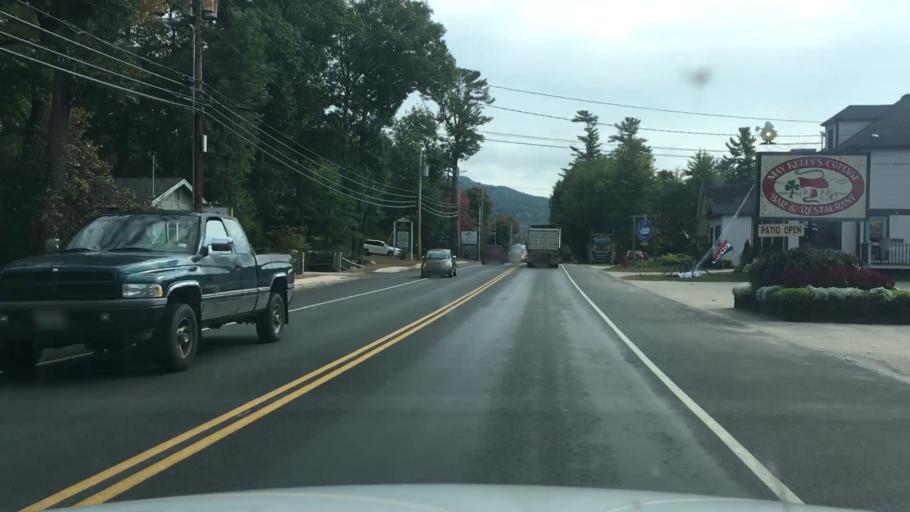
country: US
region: New Hampshire
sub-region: Carroll County
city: North Conway
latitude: 44.0593
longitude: -71.1366
